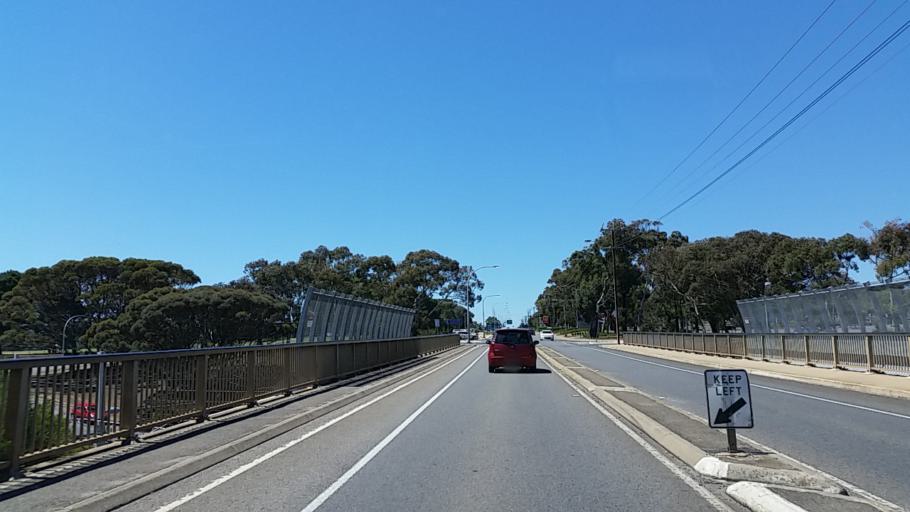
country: AU
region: South Australia
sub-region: Onkaparinga
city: Noarlunga Downs
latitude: -35.1383
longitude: 138.4928
